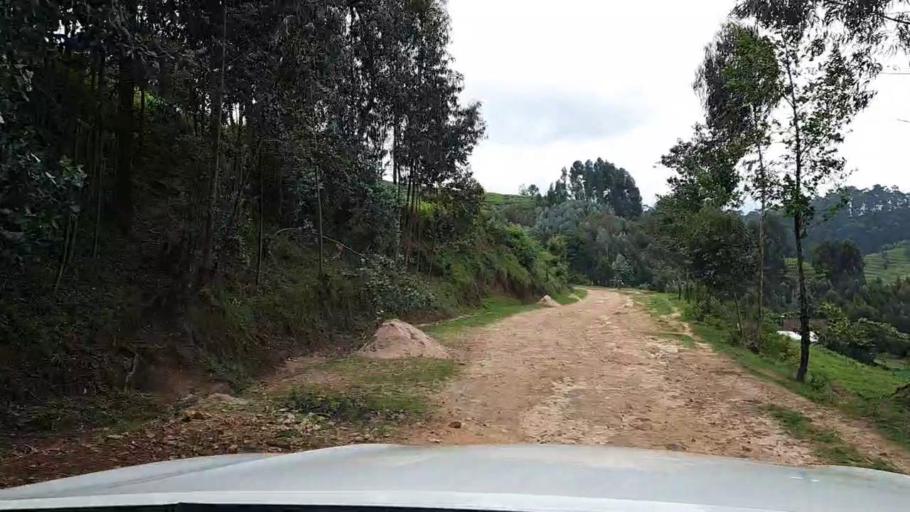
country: RW
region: Western Province
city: Kibuye
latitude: -2.2862
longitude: 29.3694
